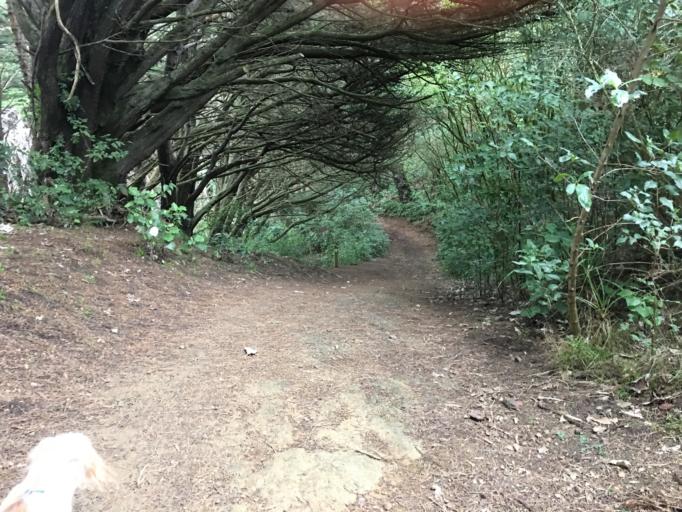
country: NZ
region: Wellington
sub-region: Wellington City
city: Kelburn
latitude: -41.2706
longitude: 174.7687
